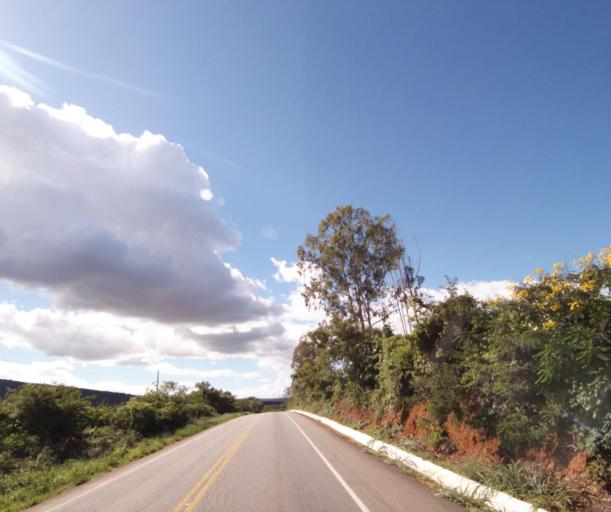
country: BR
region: Bahia
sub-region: Caetite
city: Caetite
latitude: -14.0840
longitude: -42.4512
